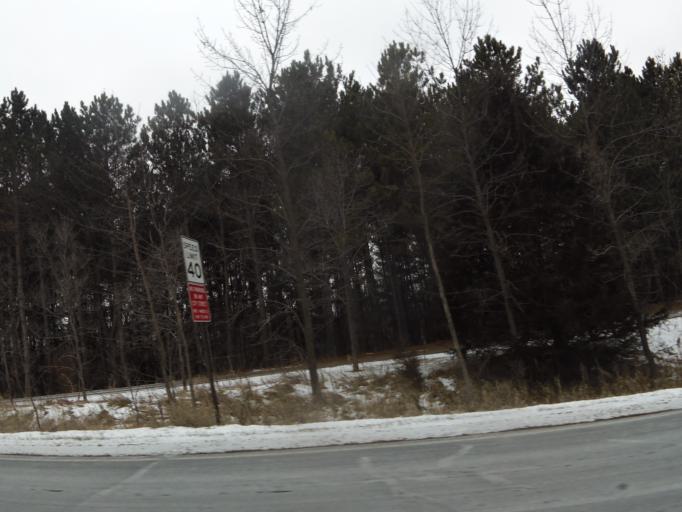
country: US
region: Minnesota
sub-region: Hennepin County
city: Medina
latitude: 45.0175
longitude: -93.5837
